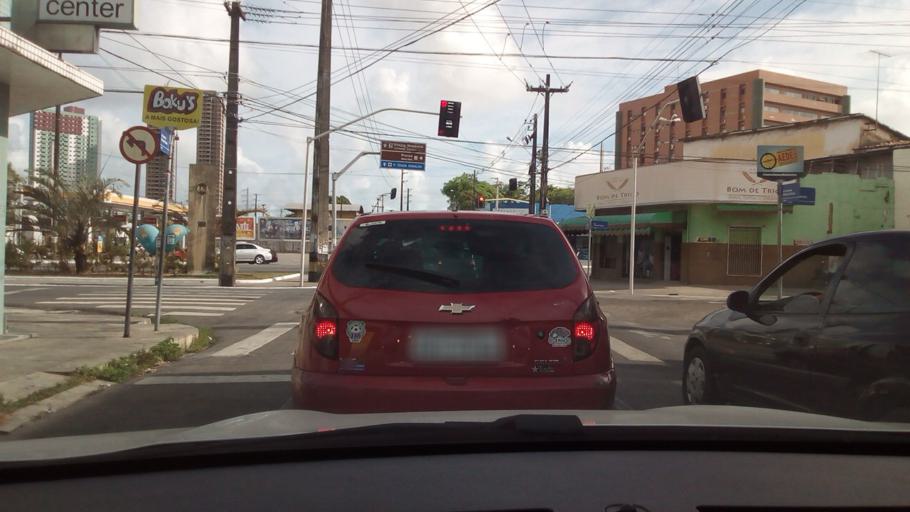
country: BR
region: Paraiba
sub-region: Joao Pessoa
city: Joao Pessoa
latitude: -7.1203
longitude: -34.8674
